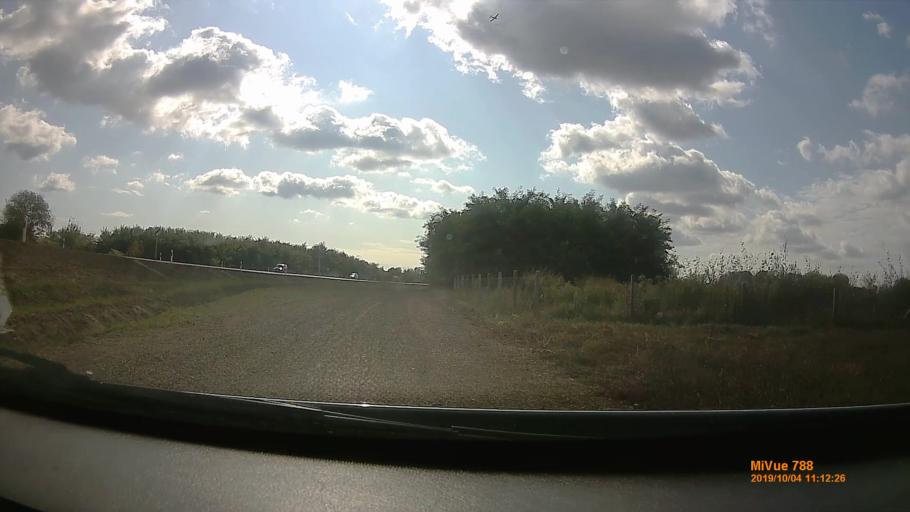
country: HU
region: Szabolcs-Szatmar-Bereg
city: Nyirtelek
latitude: 47.9992
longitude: 21.6732
